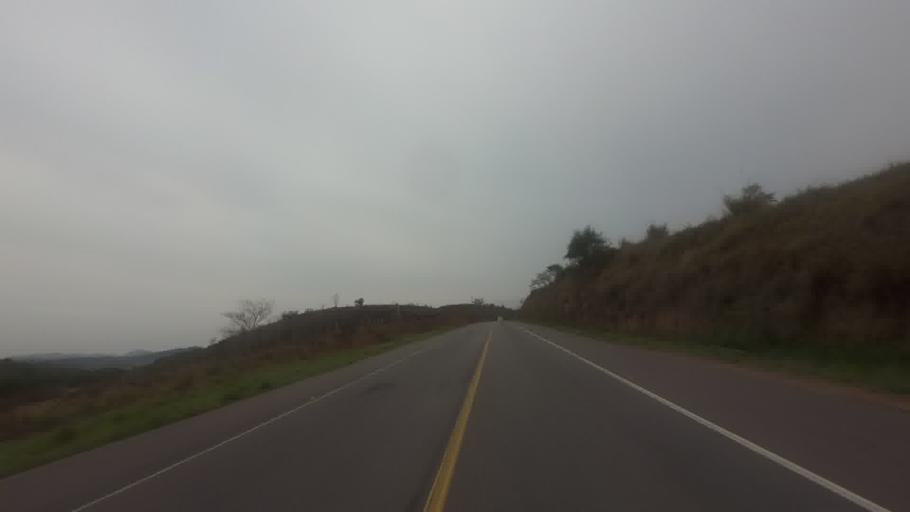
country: BR
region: Minas Gerais
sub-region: Recreio
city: Recreio
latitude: -21.6744
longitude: -42.3927
